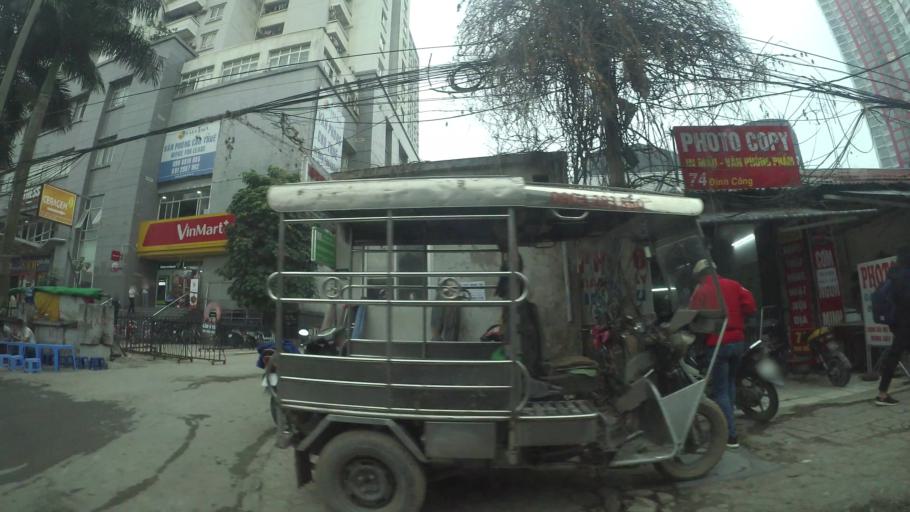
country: VN
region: Ha Noi
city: Hai BaTrung
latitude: 20.9847
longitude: 105.8391
